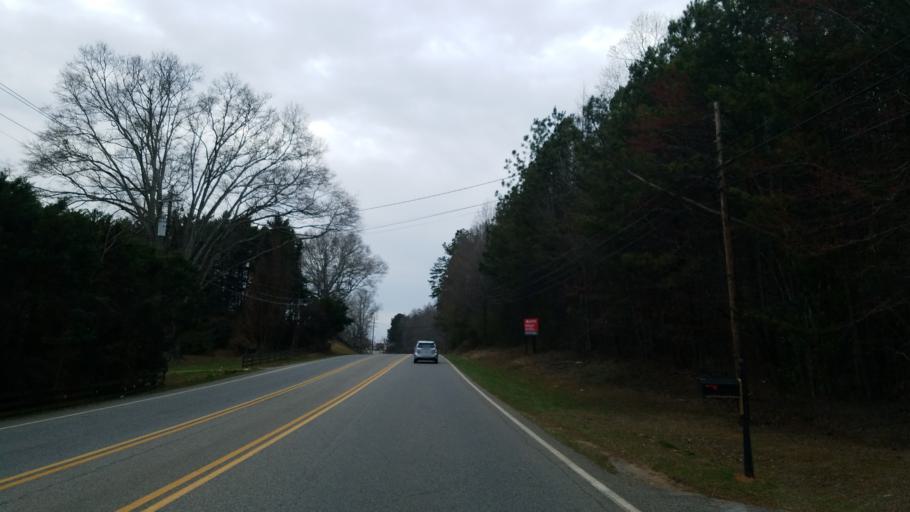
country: US
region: Georgia
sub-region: Cherokee County
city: Canton
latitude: 34.2785
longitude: -84.4463
